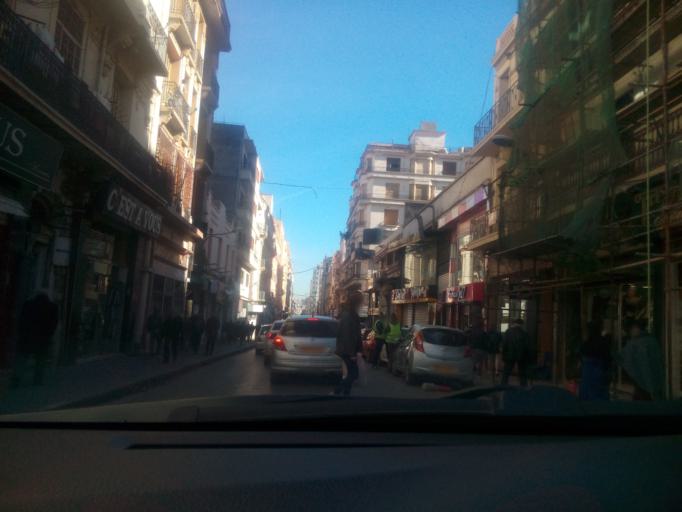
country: DZ
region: Oran
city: Oran
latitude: 35.7015
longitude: -0.6457
